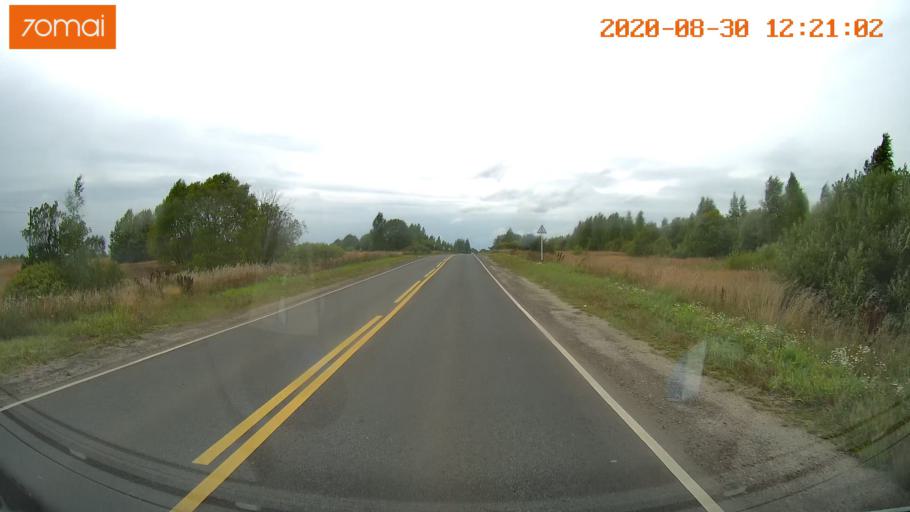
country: RU
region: Ivanovo
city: Yur'yevets
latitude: 57.3237
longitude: 42.8853
